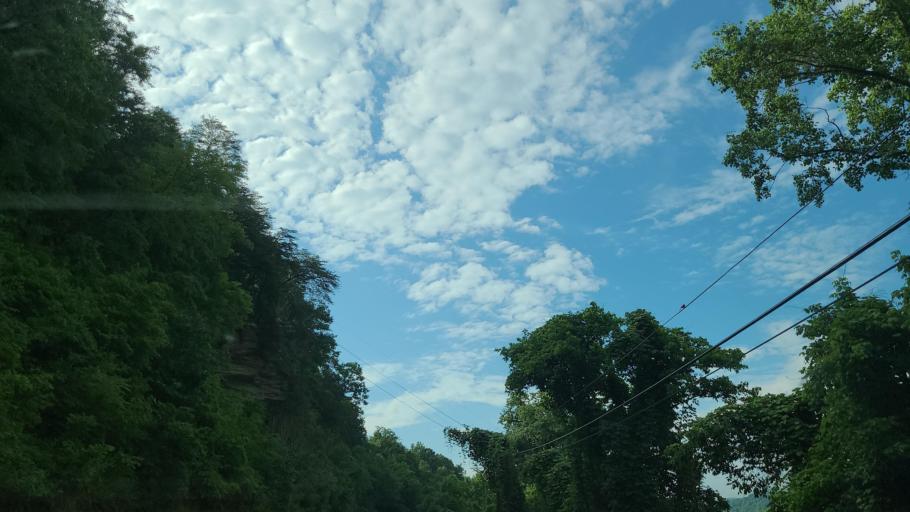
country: US
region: Kentucky
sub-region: Whitley County
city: Williamsburg
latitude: 36.7376
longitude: -84.1320
